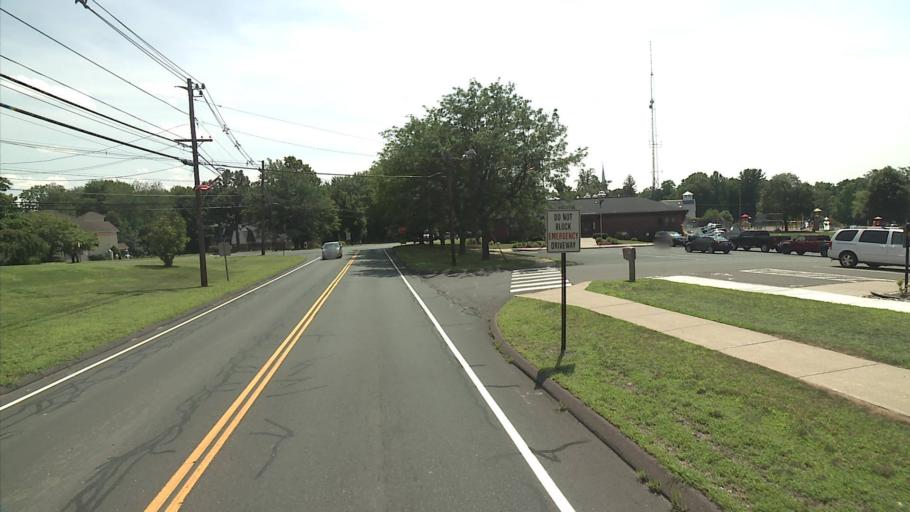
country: US
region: Connecticut
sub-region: Tolland County
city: Rockville
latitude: 41.8402
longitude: -72.4647
